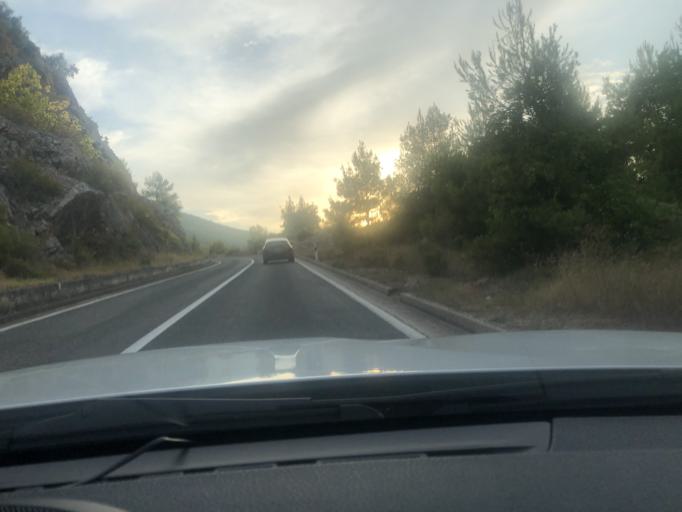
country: HR
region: Splitsko-Dalmatinska
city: Stari Grad
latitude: 43.1675
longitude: 16.5622
